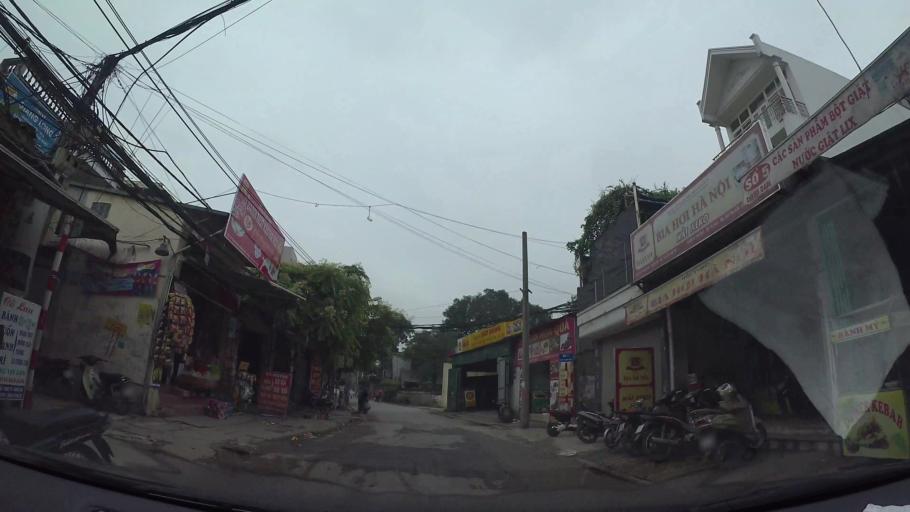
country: VN
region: Ha Noi
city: Hai BaTrung
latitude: 20.9932
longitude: 105.8908
